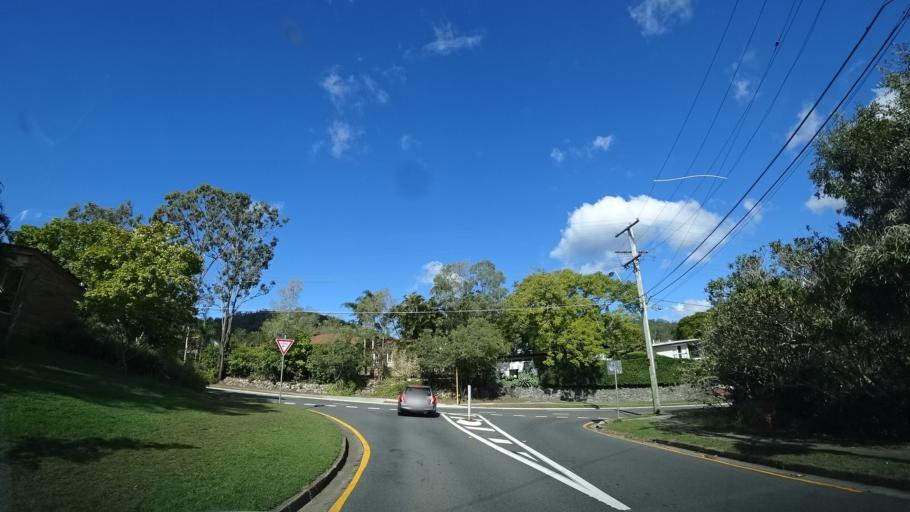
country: AU
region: Queensland
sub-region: Brisbane
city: Taringa
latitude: -27.4484
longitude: 152.9573
